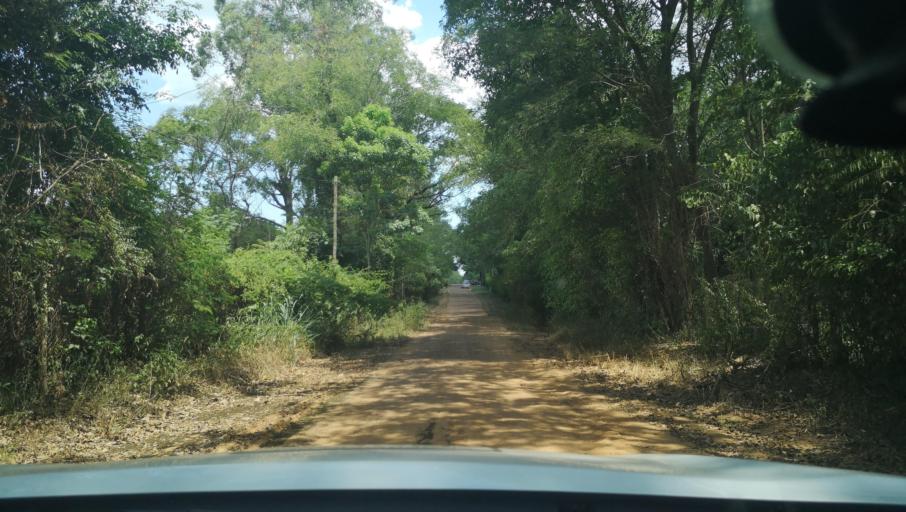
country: PY
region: Itapua
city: Carmen del Parana
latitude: -27.1510
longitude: -56.2480
